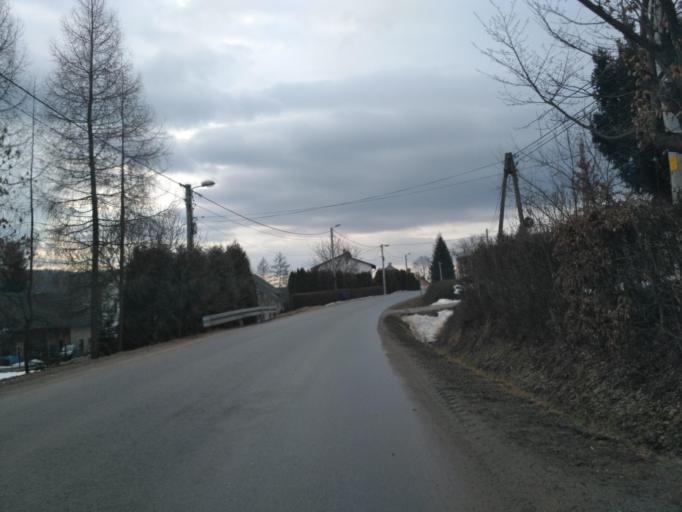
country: PL
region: Subcarpathian Voivodeship
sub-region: Powiat brzozowski
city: Dydnia
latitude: 49.6269
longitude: 22.1589
